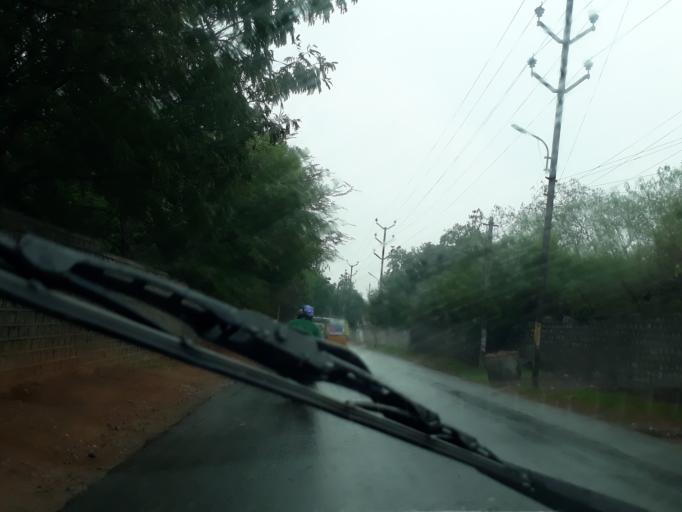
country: IN
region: Telangana
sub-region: Hyderabad
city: Malkajgiri
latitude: 17.4672
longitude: 78.5042
